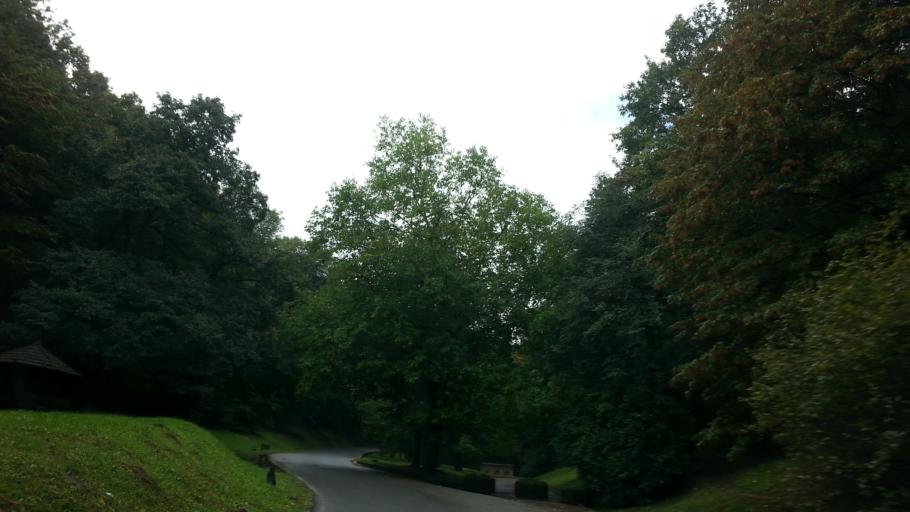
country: RS
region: Central Serbia
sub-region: Belgrade
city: Savski Venac
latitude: 44.7666
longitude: 20.4362
